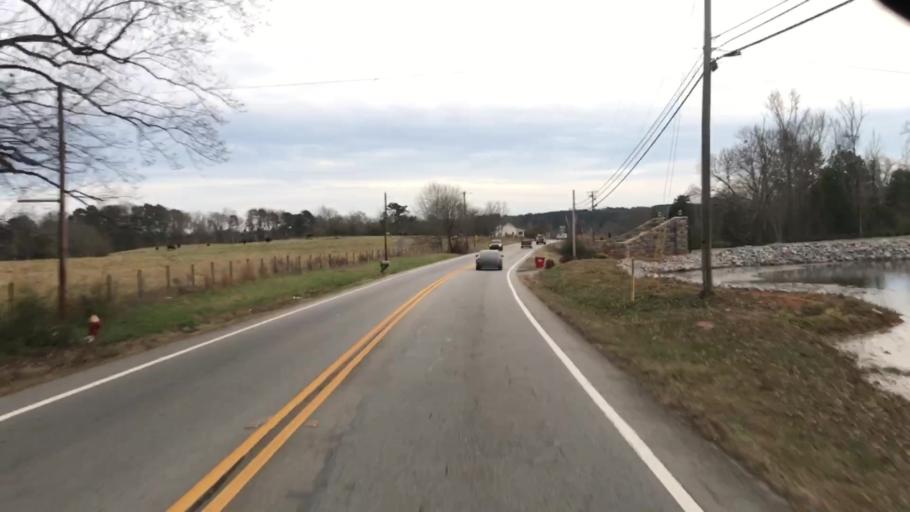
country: US
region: Georgia
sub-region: Barrow County
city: Winder
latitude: 34.0163
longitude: -83.7595
